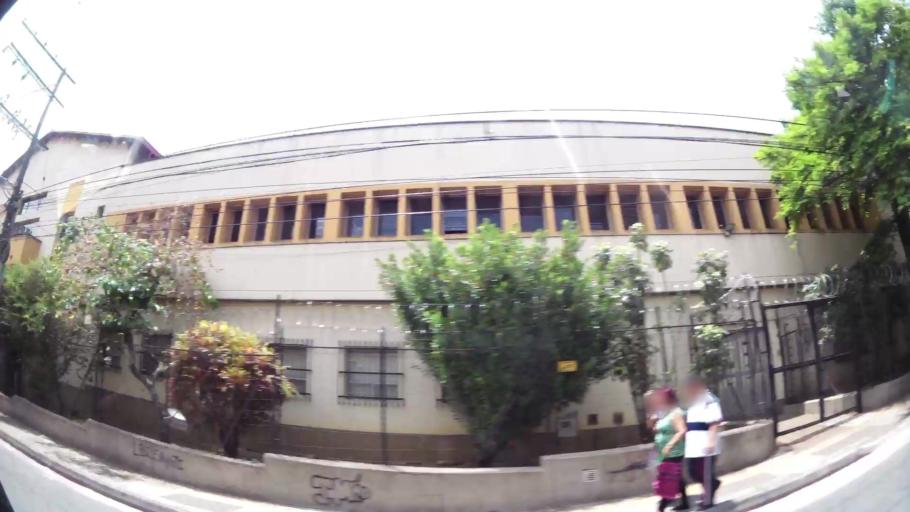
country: CO
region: Antioquia
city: Bello
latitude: 6.3325
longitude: -75.5583
